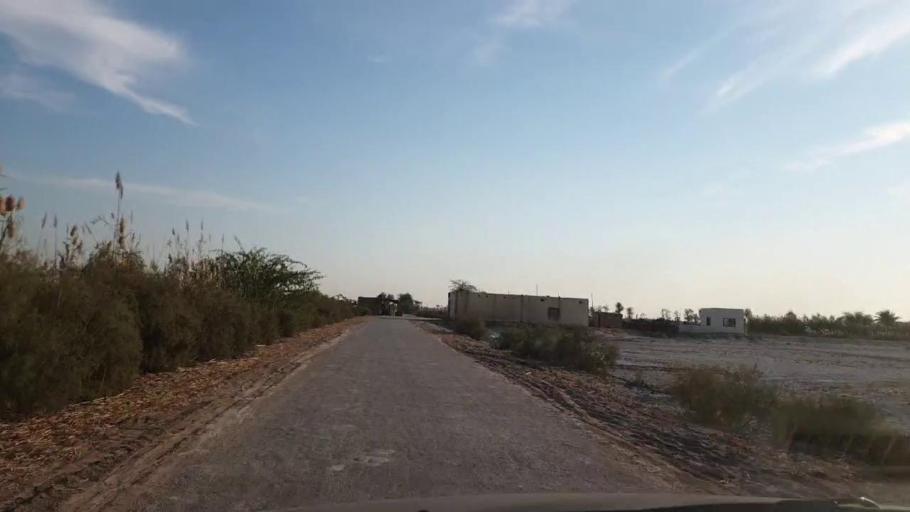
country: PK
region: Sindh
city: Khadro
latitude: 26.1608
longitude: 68.7535
